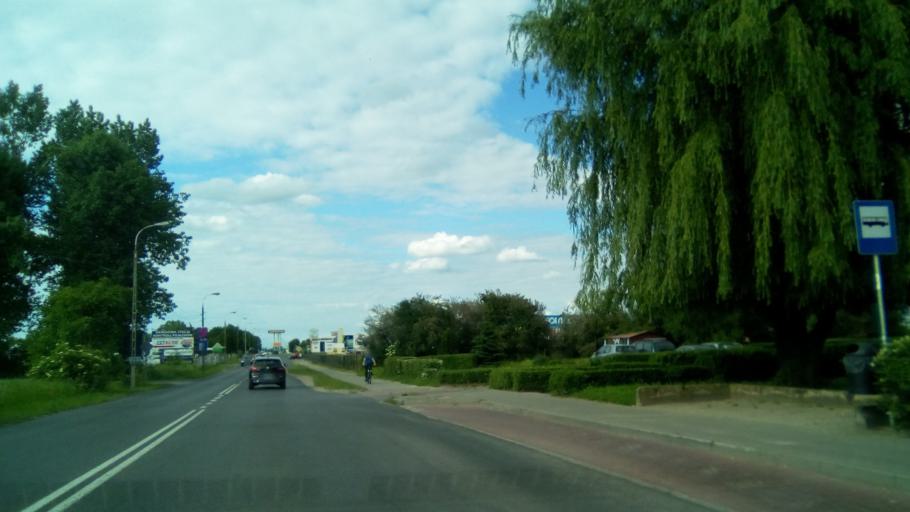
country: PL
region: Greater Poland Voivodeship
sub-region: Powiat gnieznienski
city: Gniezno
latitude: 52.5571
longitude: 17.6073
